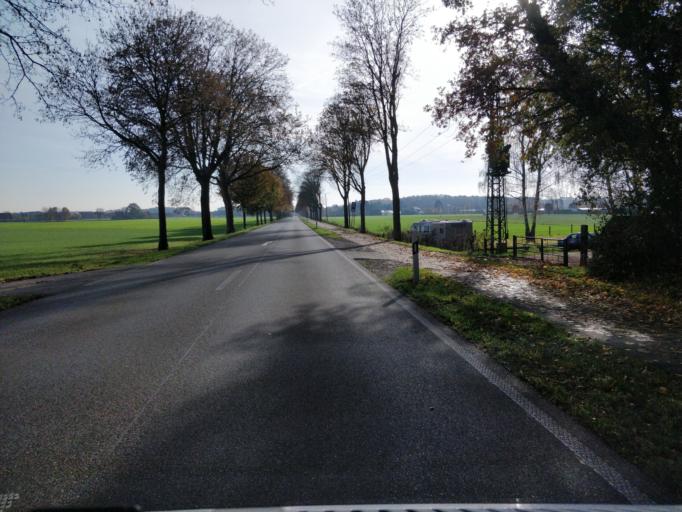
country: DE
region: North Rhine-Westphalia
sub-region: Regierungsbezirk Dusseldorf
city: Mehrhoog
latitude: 51.7455
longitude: 6.4921
